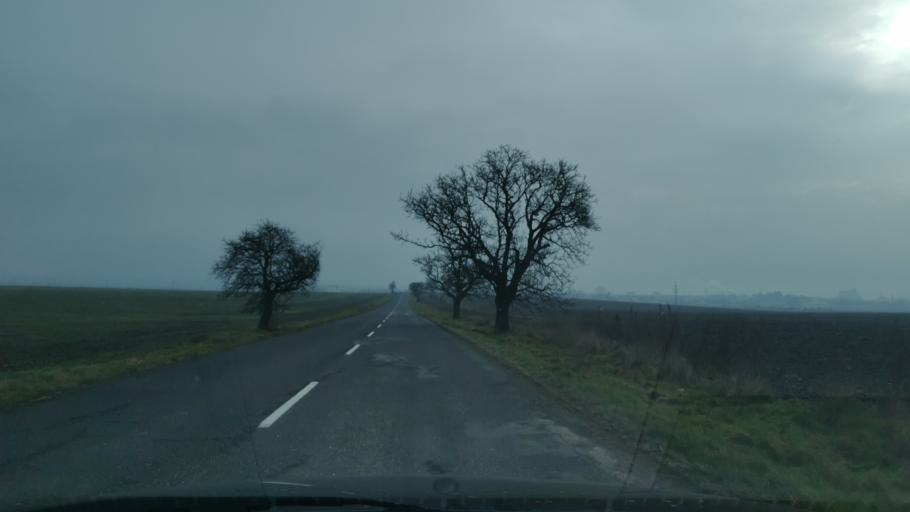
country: SK
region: Trnavsky
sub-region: Okres Senica
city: Senica
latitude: 48.6983
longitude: 17.3476
